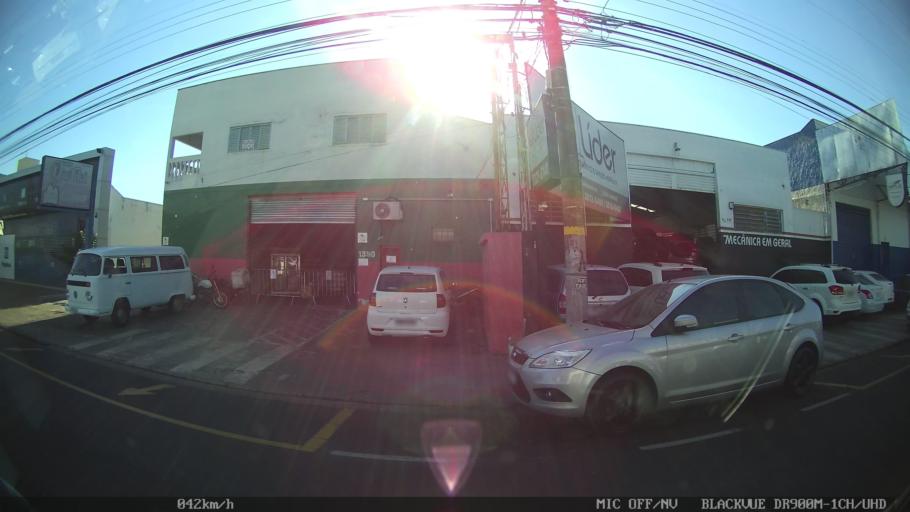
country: BR
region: Sao Paulo
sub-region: Sao Jose Do Rio Preto
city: Sao Jose do Rio Preto
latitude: -20.7931
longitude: -49.3629
